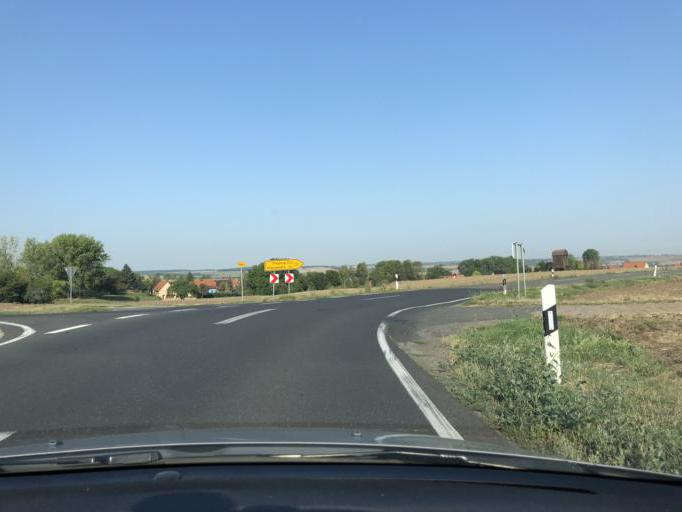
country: DE
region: Saxony-Anhalt
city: Goseck
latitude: 51.2353
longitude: 11.8870
